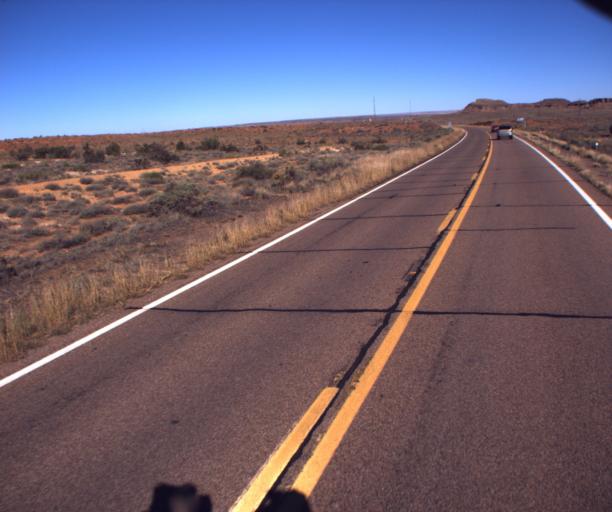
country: US
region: Arizona
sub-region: Navajo County
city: Holbrook
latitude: 34.8521
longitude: -110.1487
